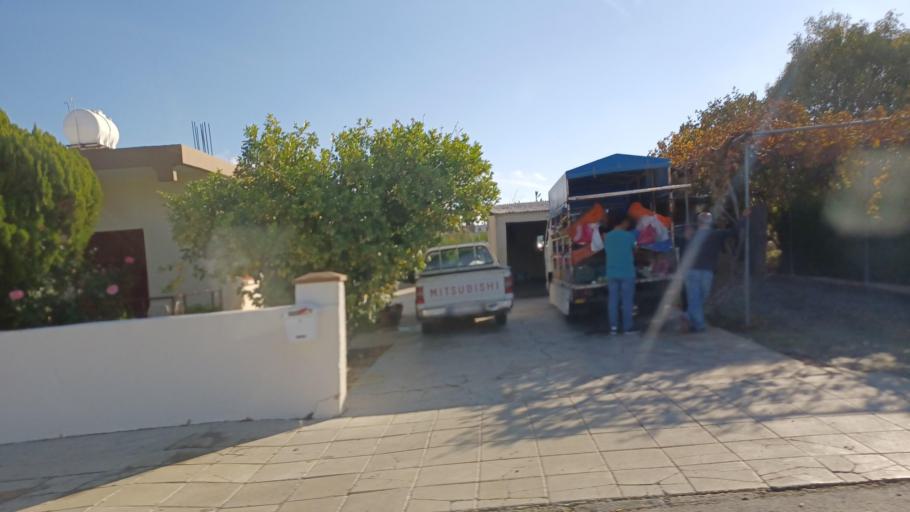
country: CY
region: Larnaka
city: Athienou
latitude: 35.0554
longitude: 33.5375
